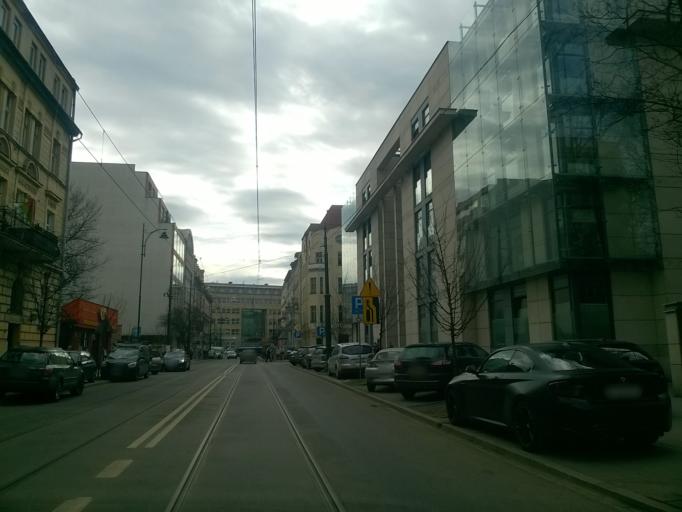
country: PL
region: Lesser Poland Voivodeship
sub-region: Krakow
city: Krakow
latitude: 50.0667
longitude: 19.9520
